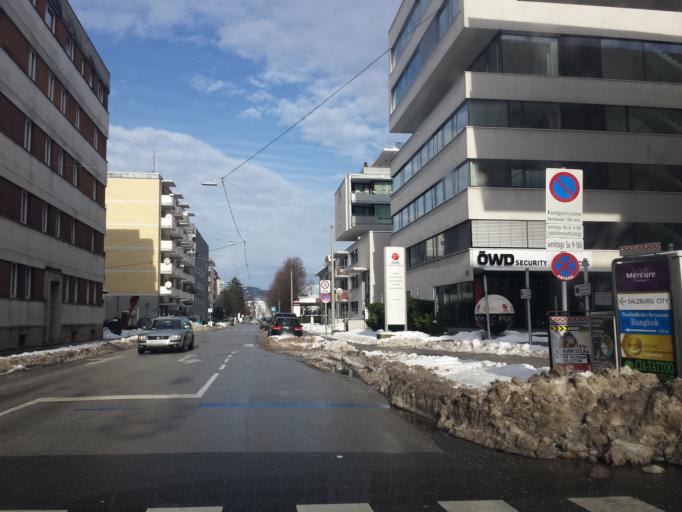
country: AT
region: Salzburg
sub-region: Salzburg Stadt
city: Salzburg
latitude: 47.8086
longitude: 13.0510
